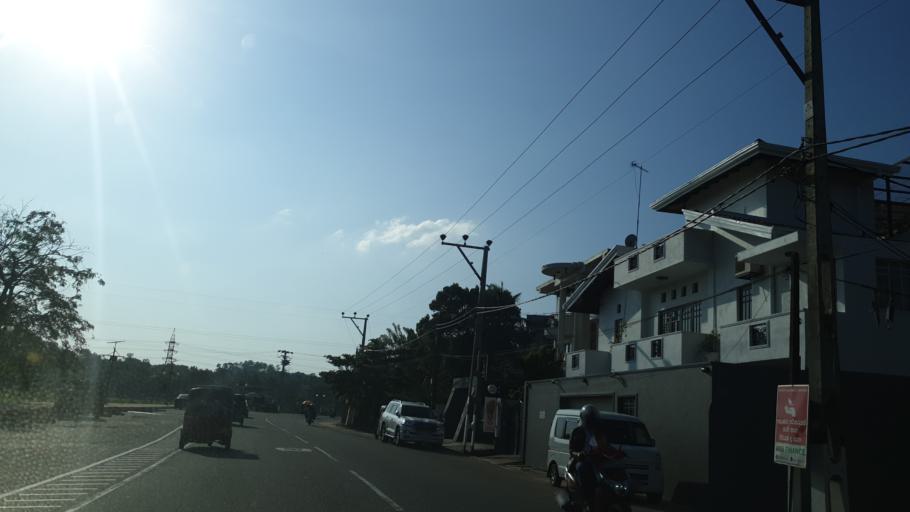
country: LK
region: Western
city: Battaramulla South
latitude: 6.8760
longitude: 79.9304
